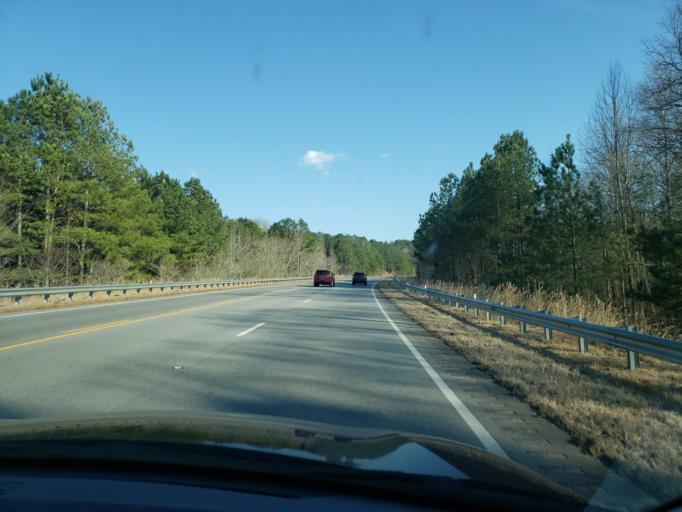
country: US
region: Alabama
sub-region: Cleburne County
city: Heflin
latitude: 33.5027
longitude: -85.6072
